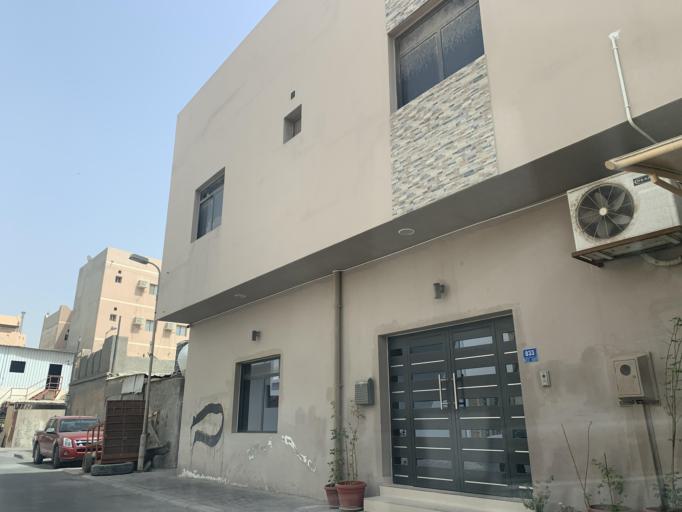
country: BH
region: Northern
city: Madinat `Isa
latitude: 26.1824
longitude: 50.5236
